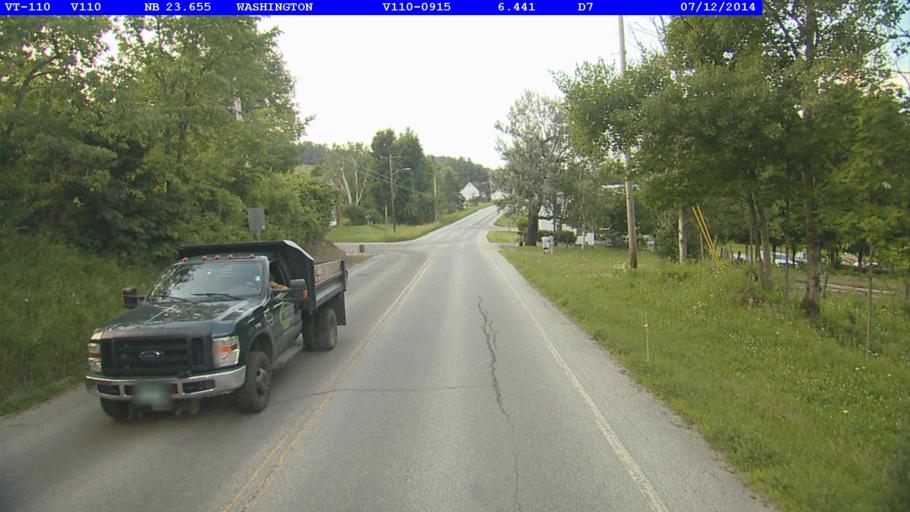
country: US
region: Vermont
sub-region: Washington County
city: South Barre
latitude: 44.1163
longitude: -72.4335
